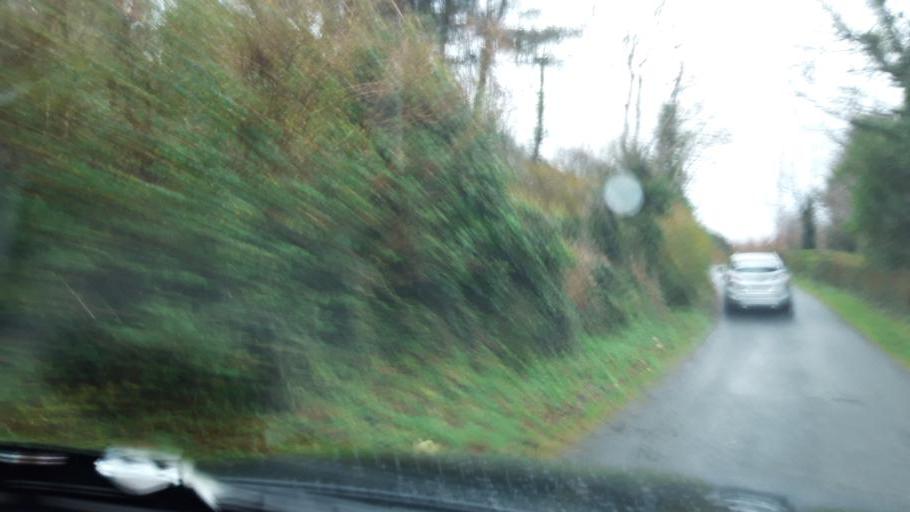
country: IE
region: Ulster
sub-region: County Donegal
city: Buncrana
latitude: 55.2222
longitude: -7.6121
